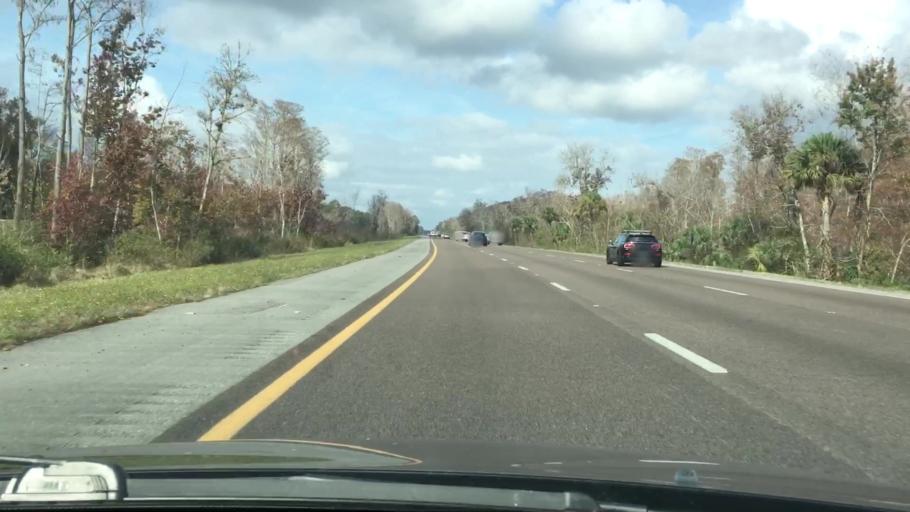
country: US
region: Florida
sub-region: Volusia County
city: Oak Hill
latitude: 28.8721
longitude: -80.9198
